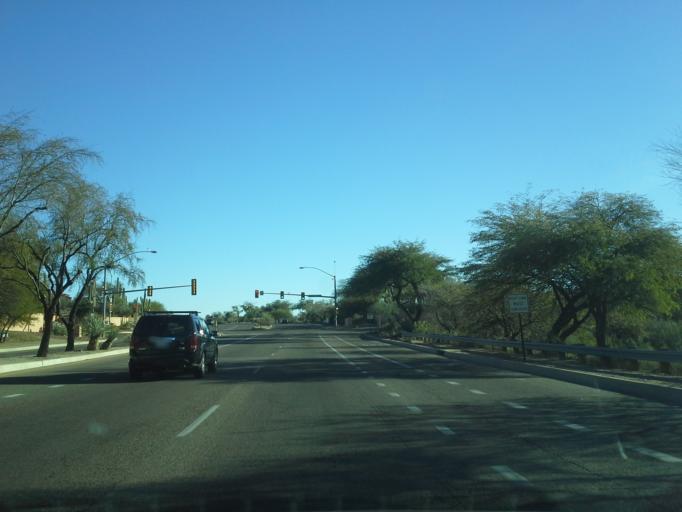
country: US
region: Arizona
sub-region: Pima County
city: Catalina Foothills
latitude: 32.3136
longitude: -110.9125
